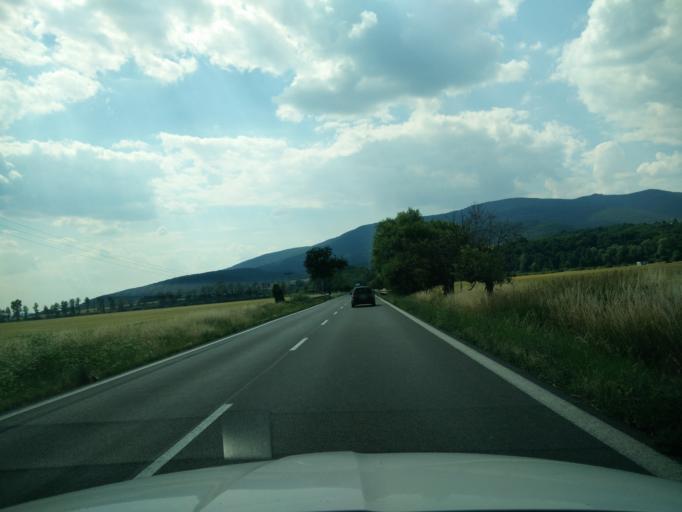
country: SK
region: Nitriansky
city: Novaky
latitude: 48.7226
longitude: 18.4888
